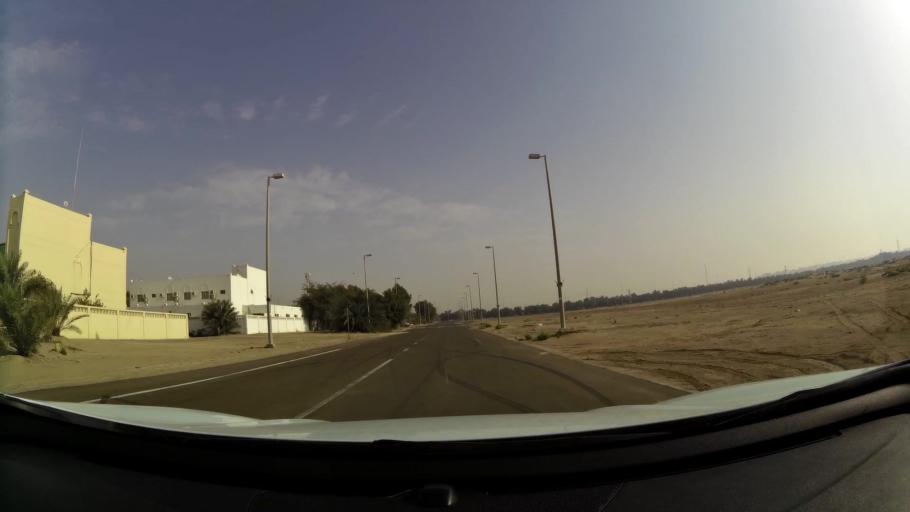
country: AE
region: Abu Dhabi
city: Abu Dhabi
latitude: 24.2609
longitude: 54.6737
